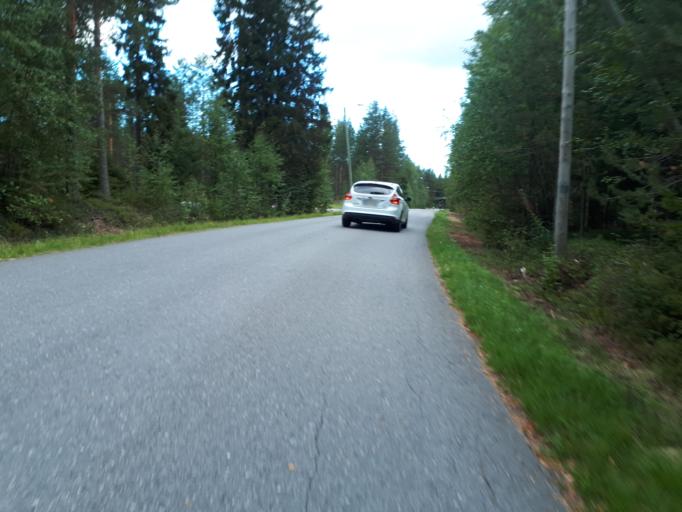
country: FI
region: Northern Ostrobothnia
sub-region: Oulunkaari
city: Ii
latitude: 65.3299
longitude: 25.3960
